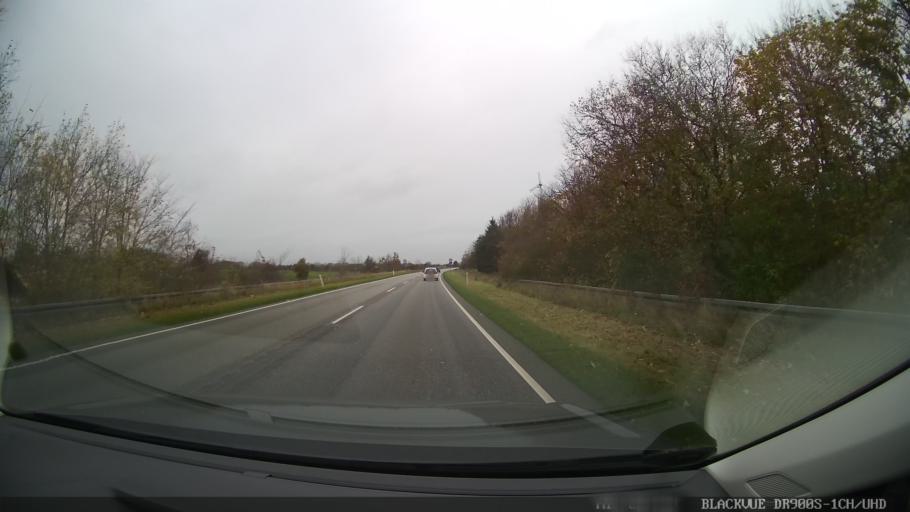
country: DK
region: North Denmark
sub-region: Thisted Kommune
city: Thisted
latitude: 56.8380
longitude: 8.7043
